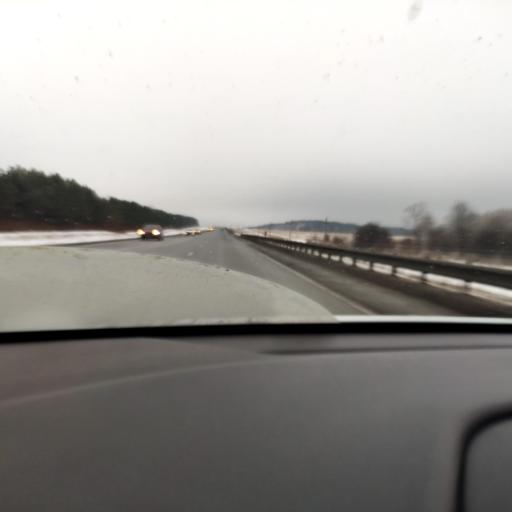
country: RU
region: Tatarstan
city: Sviyazhsk
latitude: 55.7265
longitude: 48.8170
